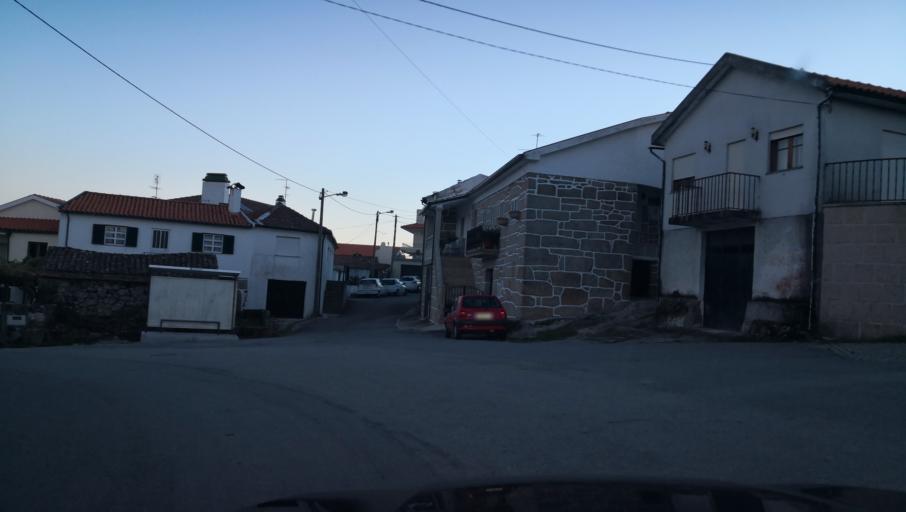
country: PT
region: Vila Real
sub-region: Santa Marta de Penaguiao
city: Santa Marta de Penaguiao
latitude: 41.2621
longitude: -7.7898
